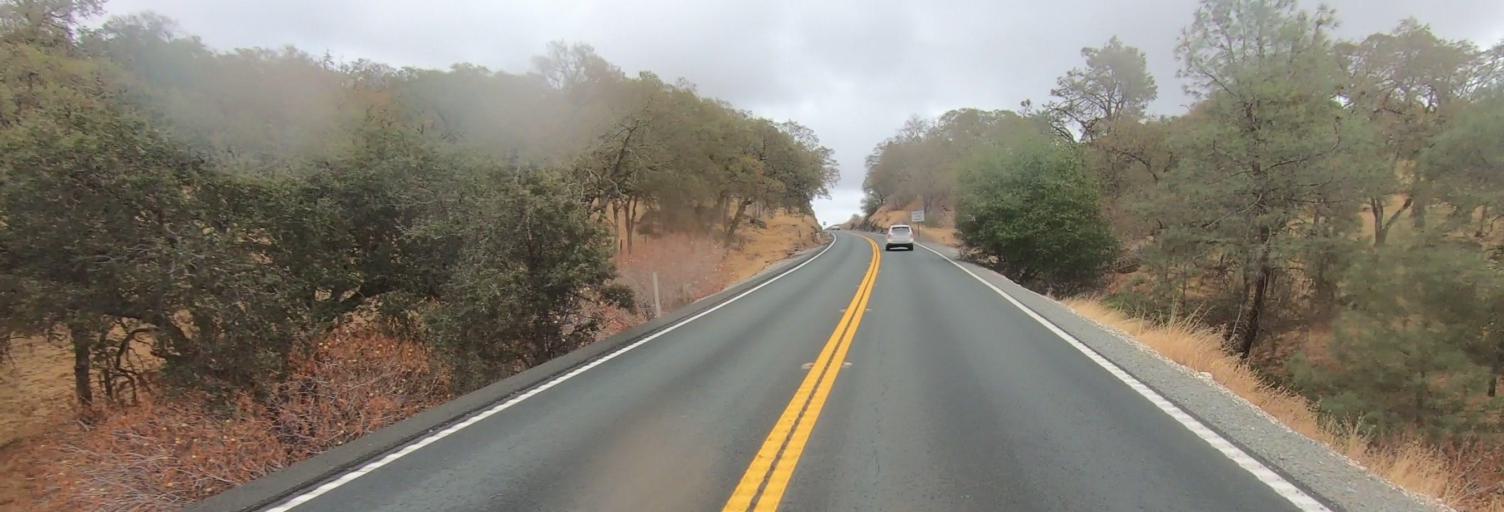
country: US
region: California
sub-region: Calaveras County
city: Valley Springs
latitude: 38.2086
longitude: -120.7779
